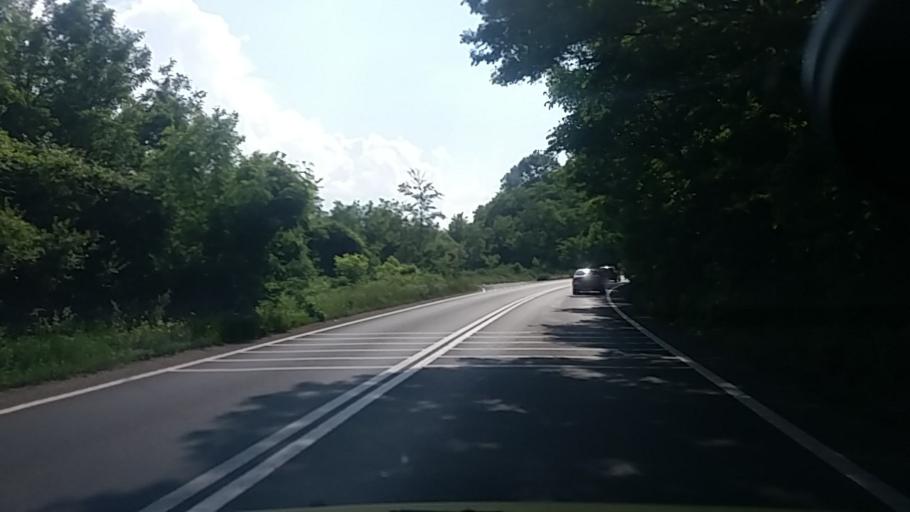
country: RO
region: Arad
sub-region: Comuna Varadia de Mures
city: Varadia de Mures
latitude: 46.0014
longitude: 22.1656
